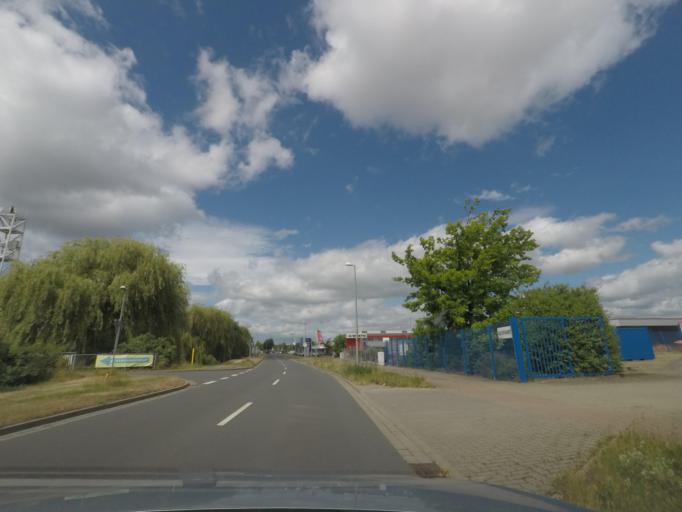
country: DE
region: Saxony-Anhalt
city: Harsleben
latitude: 51.8840
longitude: 11.0814
